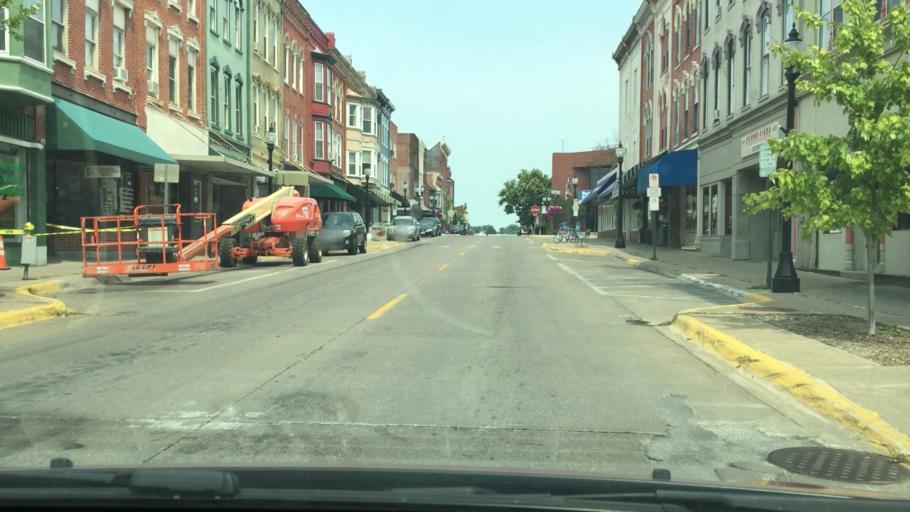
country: US
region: Iowa
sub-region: Muscatine County
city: Muscatine
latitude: 41.4219
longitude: -91.0445
